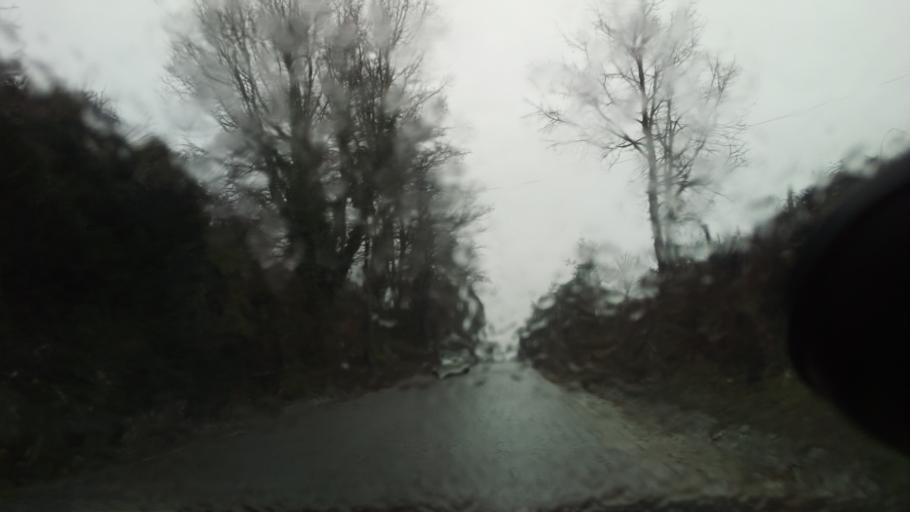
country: PT
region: Viseu
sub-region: Mangualde
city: Mangualde
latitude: 40.6074
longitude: -7.6507
